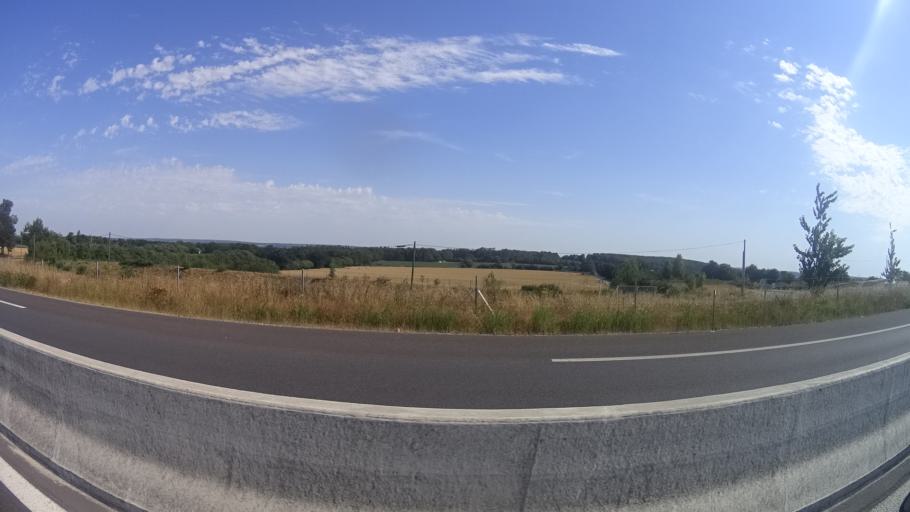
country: FR
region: Brittany
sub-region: Departement du Morbihan
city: Allaire
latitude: 47.6128
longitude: -2.1463
